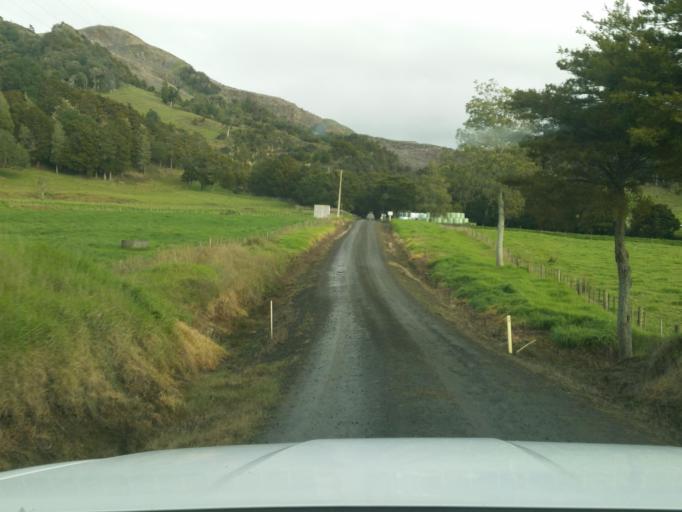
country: NZ
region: Northland
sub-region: Kaipara District
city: Dargaville
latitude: -35.7914
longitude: 173.8113
